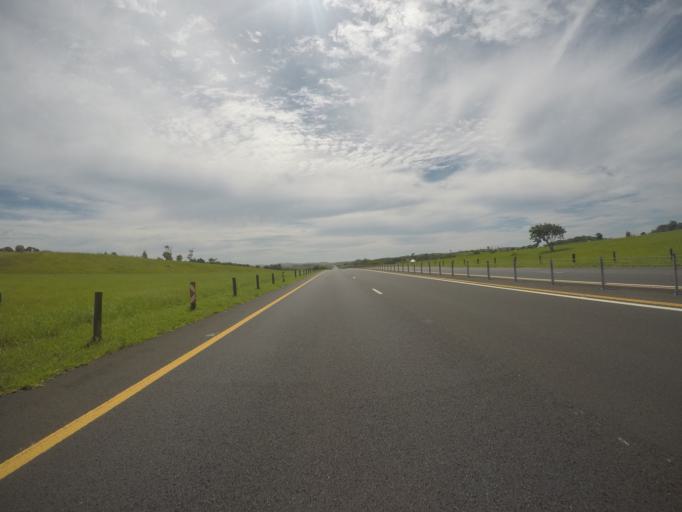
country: ZA
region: KwaZulu-Natal
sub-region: iLembe District Municipality
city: Mandeni
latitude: -29.1839
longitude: 31.4839
